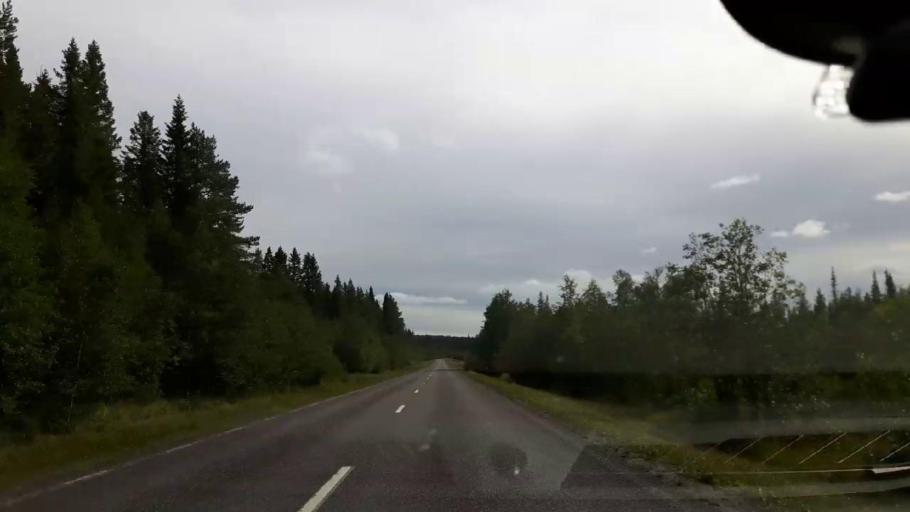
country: SE
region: Jaemtland
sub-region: Ragunda Kommun
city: Hammarstrand
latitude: 63.1315
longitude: 15.8835
